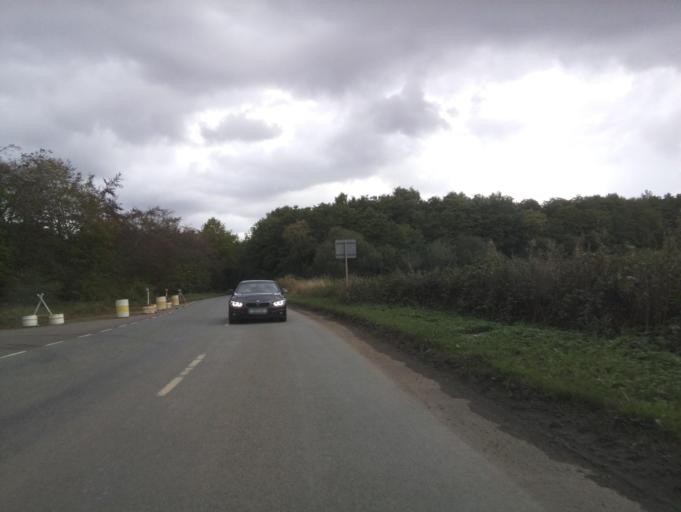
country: GB
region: England
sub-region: Staffordshire
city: Eccleshall
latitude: 52.8948
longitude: -2.2156
